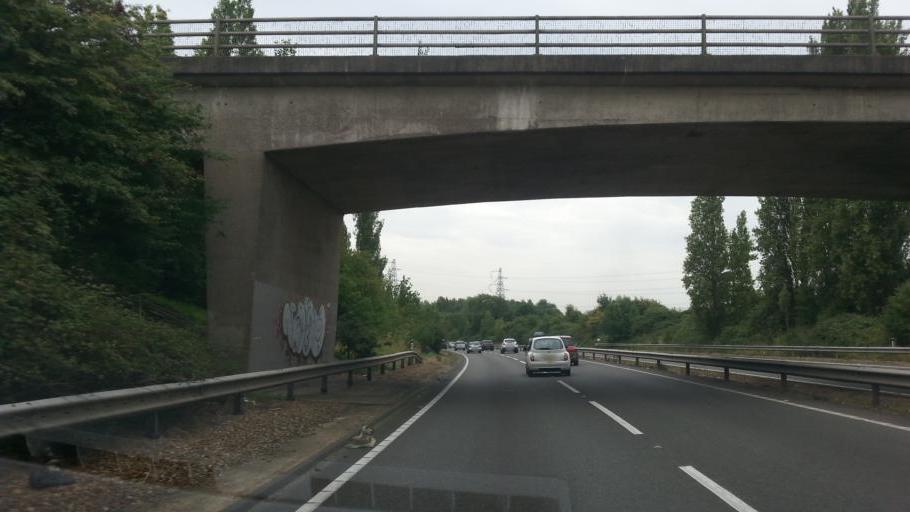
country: GB
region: England
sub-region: Cambridgeshire
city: Eaton Socon
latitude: 52.2207
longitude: -0.2988
